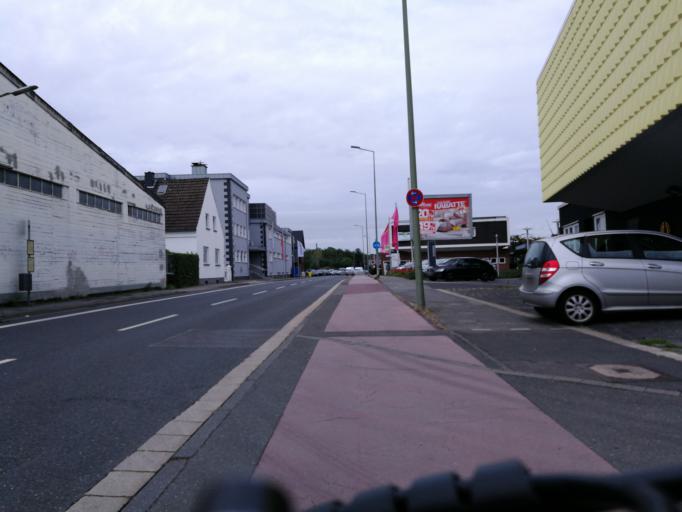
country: DE
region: North Rhine-Westphalia
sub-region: Regierungsbezirk Dusseldorf
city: Neuss
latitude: 51.1582
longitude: 6.7375
